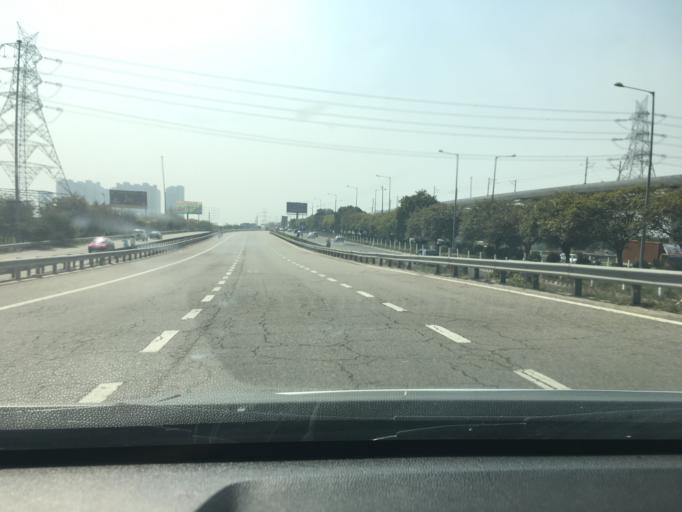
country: IN
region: Uttar Pradesh
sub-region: Gautam Buddha Nagar
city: Greater Noida
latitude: 28.4508
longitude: 77.4935
